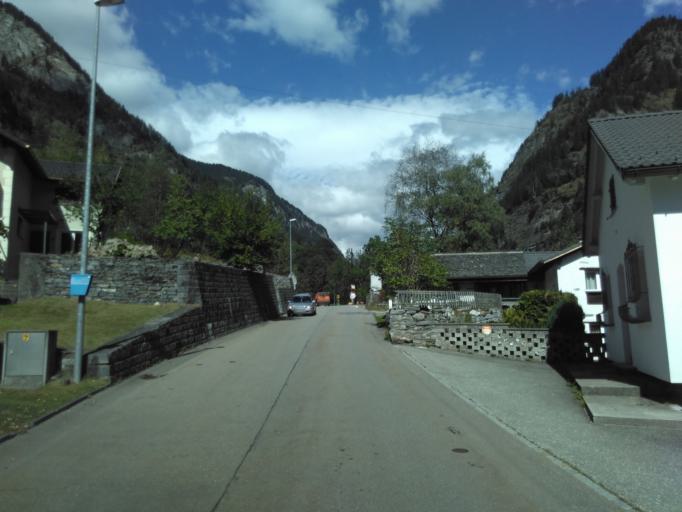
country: CH
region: Grisons
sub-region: Moesa District
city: Cauco
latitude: 46.3311
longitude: 9.1193
